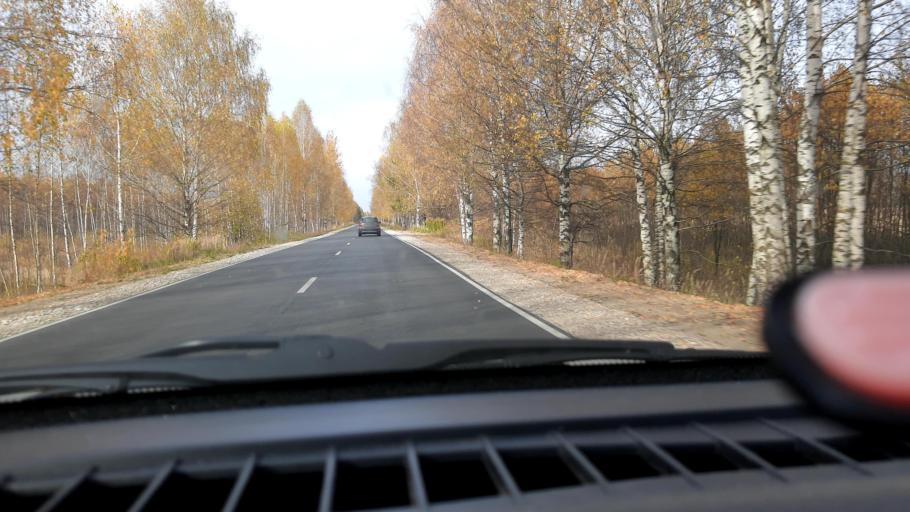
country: RU
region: Nizjnij Novgorod
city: Neklyudovo
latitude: 56.4920
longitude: 43.8593
